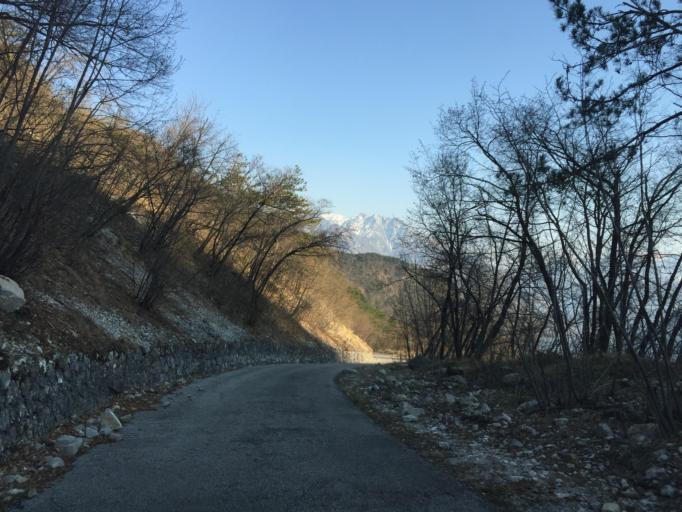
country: IT
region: Friuli Venezia Giulia
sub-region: Provincia di Udine
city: Amaro
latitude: 46.3882
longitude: 13.0798
